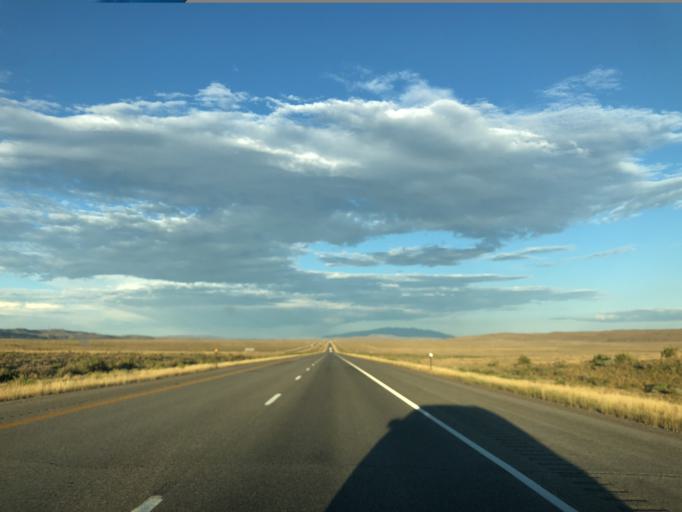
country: US
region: Wyoming
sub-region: Carbon County
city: Rawlins
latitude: 41.7697
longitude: -107.0508
